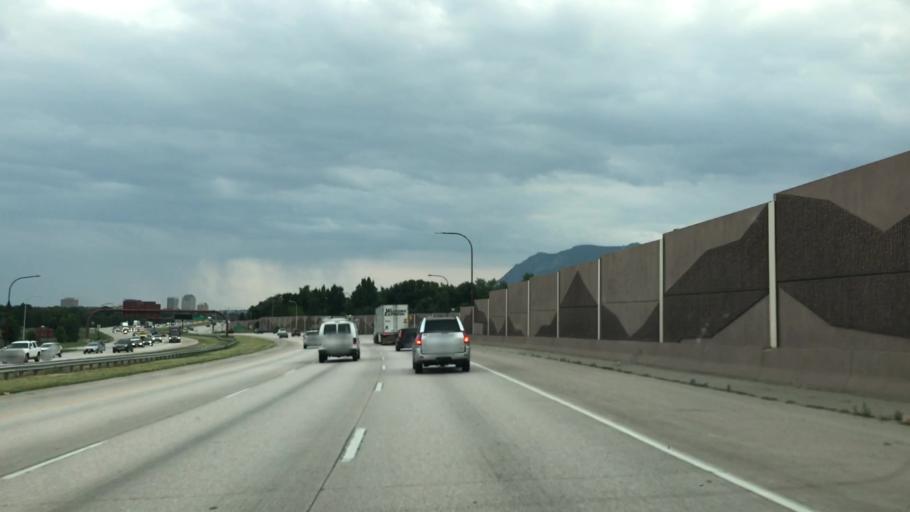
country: US
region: Colorado
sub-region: El Paso County
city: Colorado Springs
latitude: 38.8593
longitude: -104.8345
